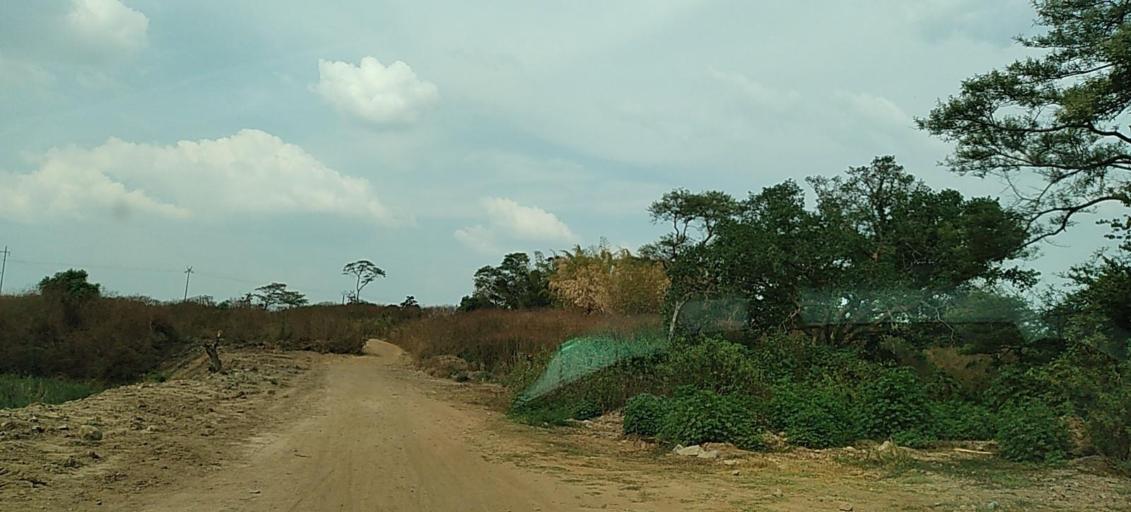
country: ZM
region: Copperbelt
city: Chililabombwe
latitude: -12.3981
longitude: 27.8032
